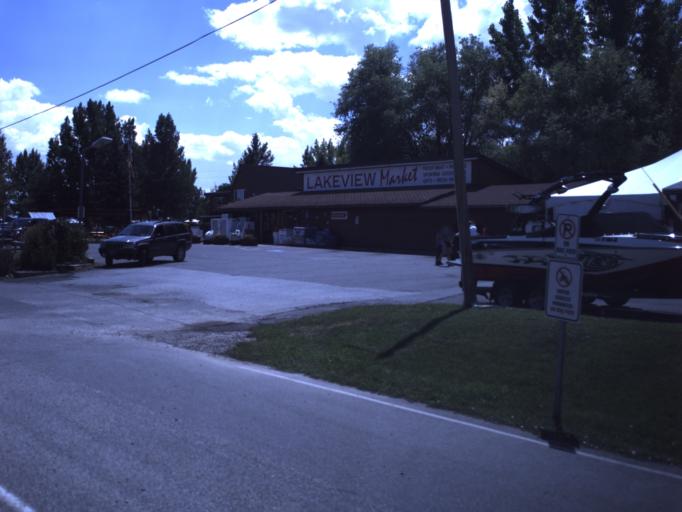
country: US
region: Idaho
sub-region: Bear Lake County
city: Paris
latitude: 41.9562
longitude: -111.3979
